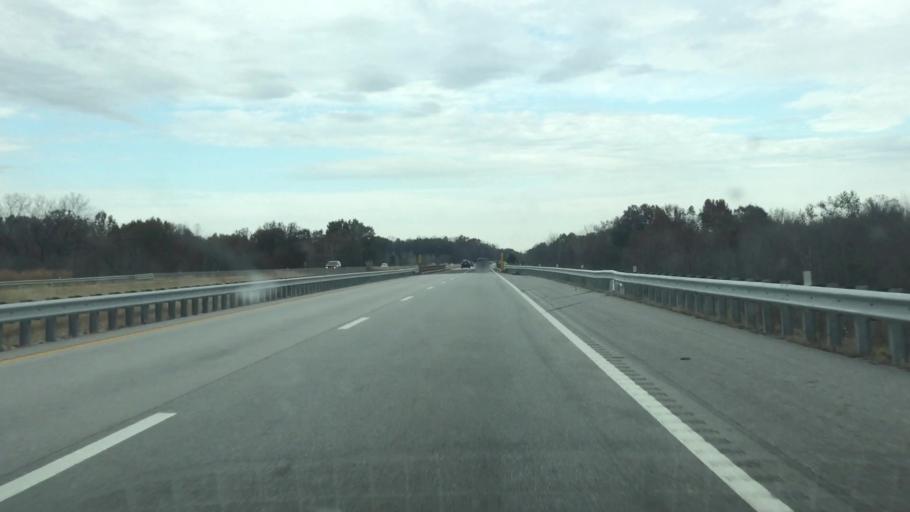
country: US
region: Missouri
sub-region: Henry County
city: Clinton
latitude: 38.2258
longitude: -93.7619
